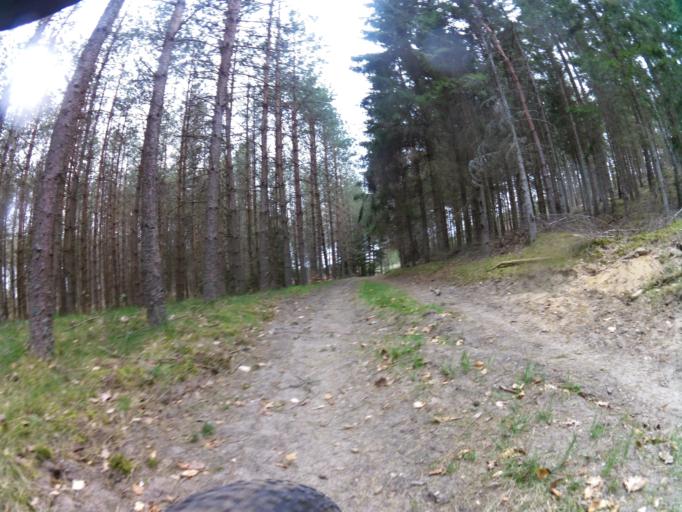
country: PL
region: West Pomeranian Voivodeship
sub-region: Powiat koszalinski
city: Polanow
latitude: 54.0605
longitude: 16.6242
